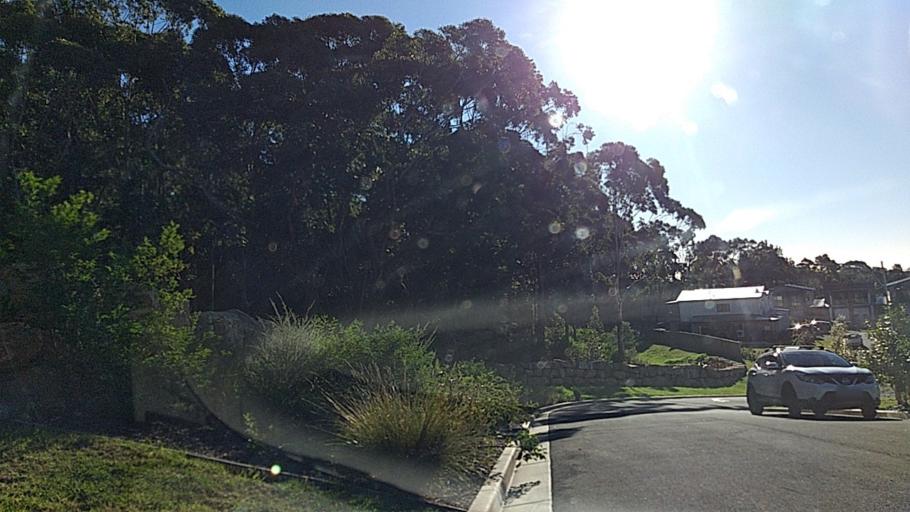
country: AU
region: New South Wales
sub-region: Wollongong
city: Bulli
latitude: -34.3318
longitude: 150.9077
